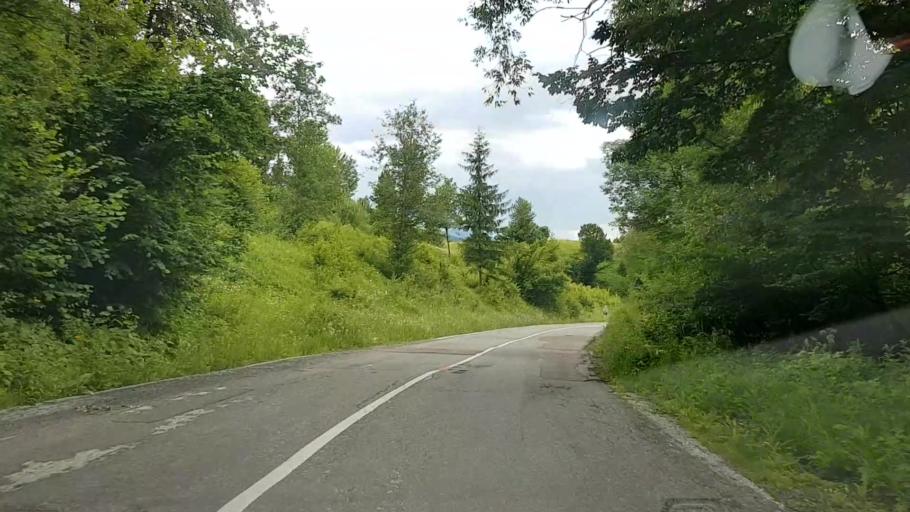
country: RO
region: Neamt
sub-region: Comuna Pangarati
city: Pangarati
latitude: 46.9567
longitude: 26.1252
